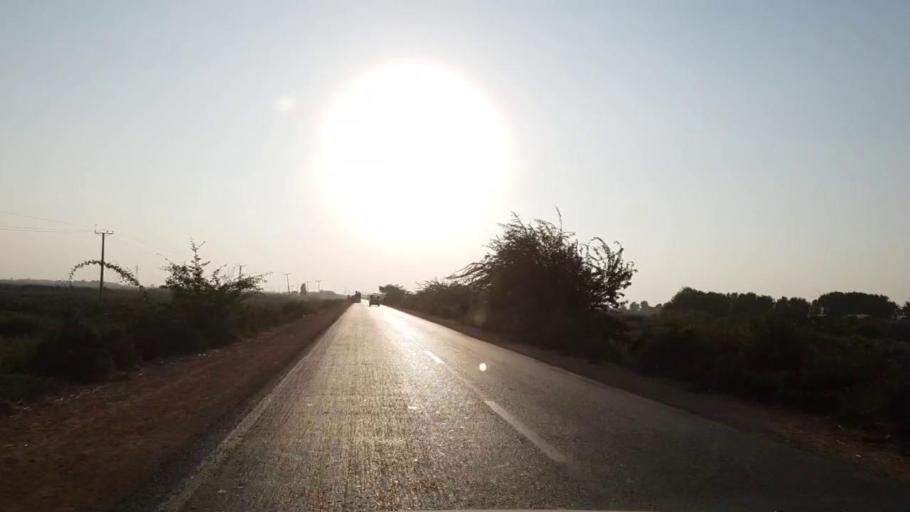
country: PK
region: Sindh
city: Daro Mehar
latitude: 24.6367
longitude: 68.1117
